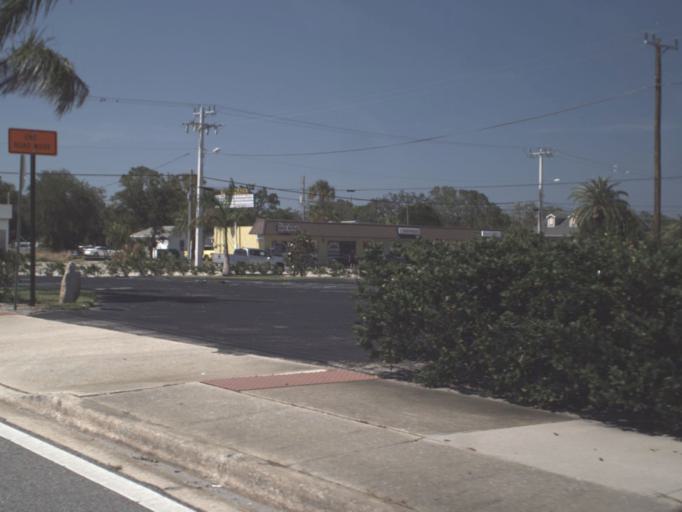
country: US
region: Florida
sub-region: Brevard County
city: Indian Harbour Beach
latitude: 28.1302
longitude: -80.6304
